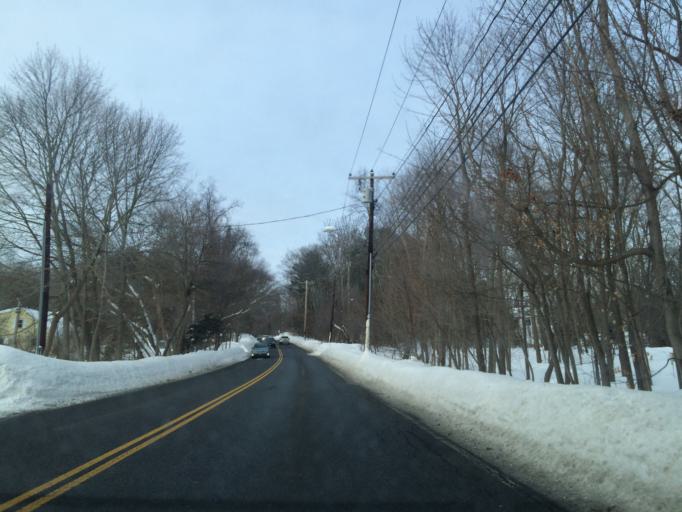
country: US
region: Massachusetts
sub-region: Middlesex County
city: Weston
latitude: 42.3406
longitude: -71.2800
